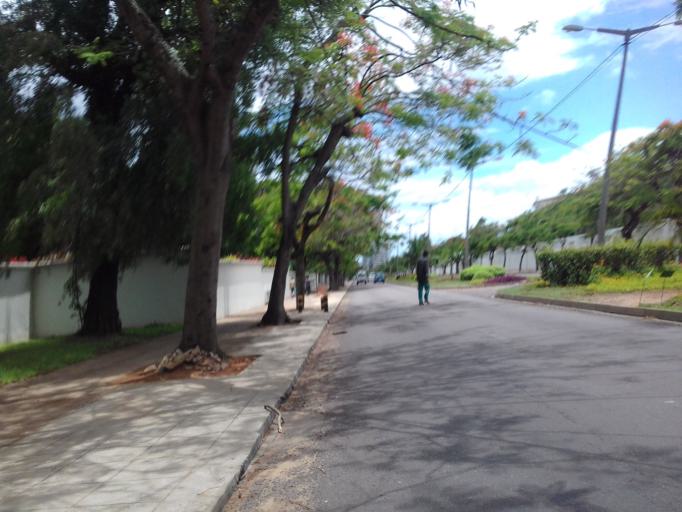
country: MZ
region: Maputo City
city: Maputo
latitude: -25.9659
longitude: 32.5989
